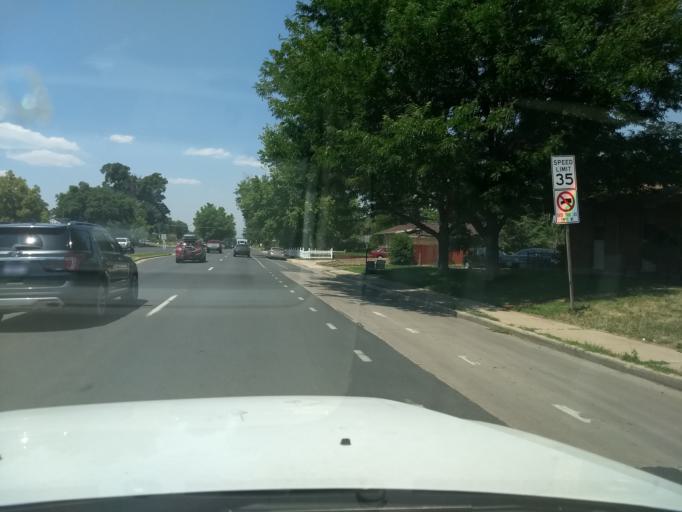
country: US
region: Colorado
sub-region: Denver County
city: Denver
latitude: 39.7620
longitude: -104.9502
